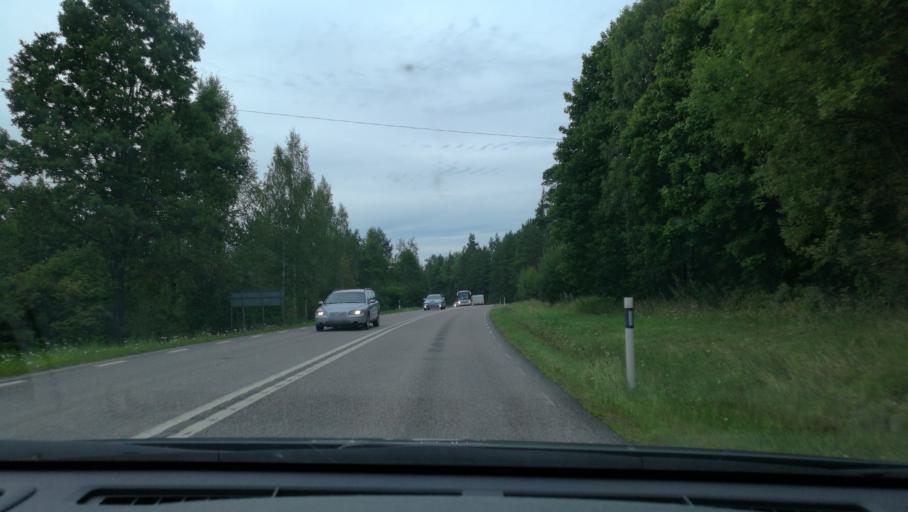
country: SE
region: Soedermanland
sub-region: Katrineholms Kommun
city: Katrineholm
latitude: 59.1454
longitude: 16.1176
